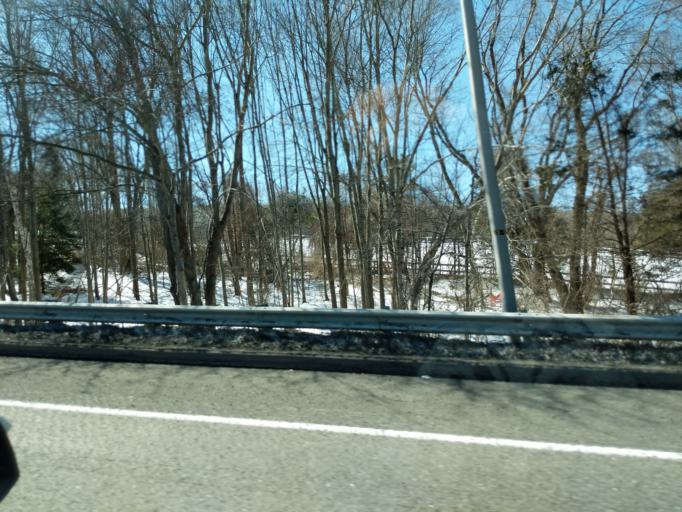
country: US
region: Rhode Island
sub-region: Providence County
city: North Smithfield
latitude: 41.9886
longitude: -71.5519
